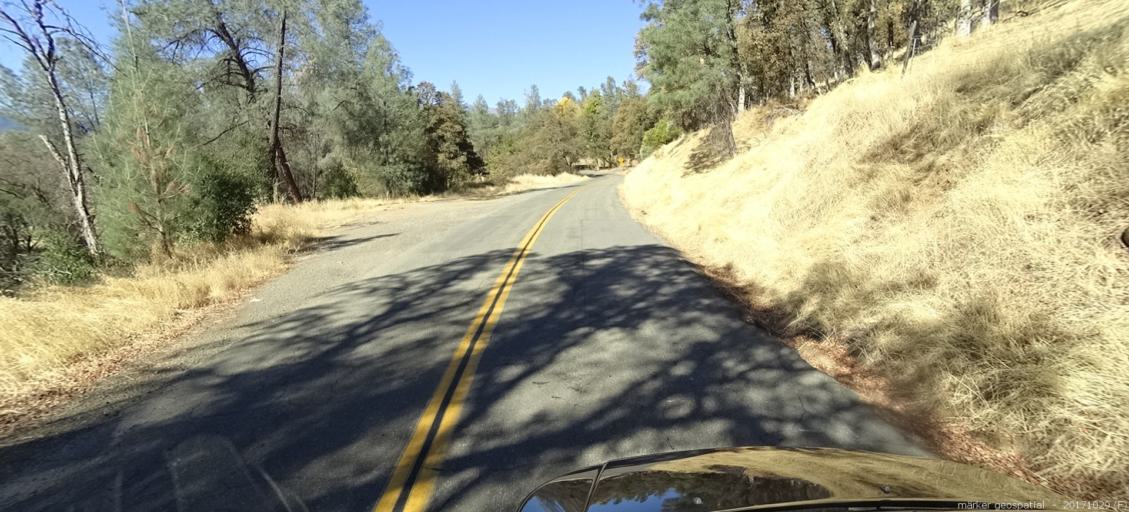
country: US
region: California
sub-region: Shasta County
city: Shasta
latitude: 40.4743
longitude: -122.6229
